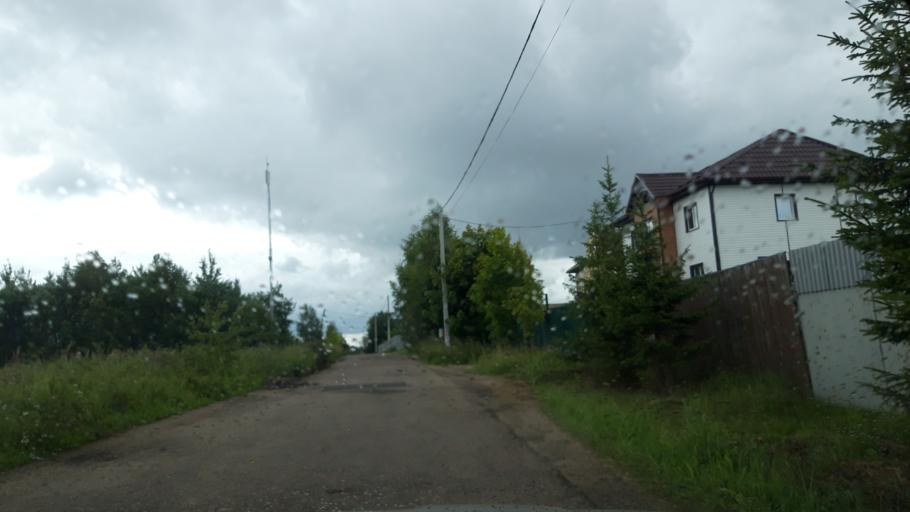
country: RU
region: Moskovskaya
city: Povarovo
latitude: 56.0955
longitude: 37.0708
